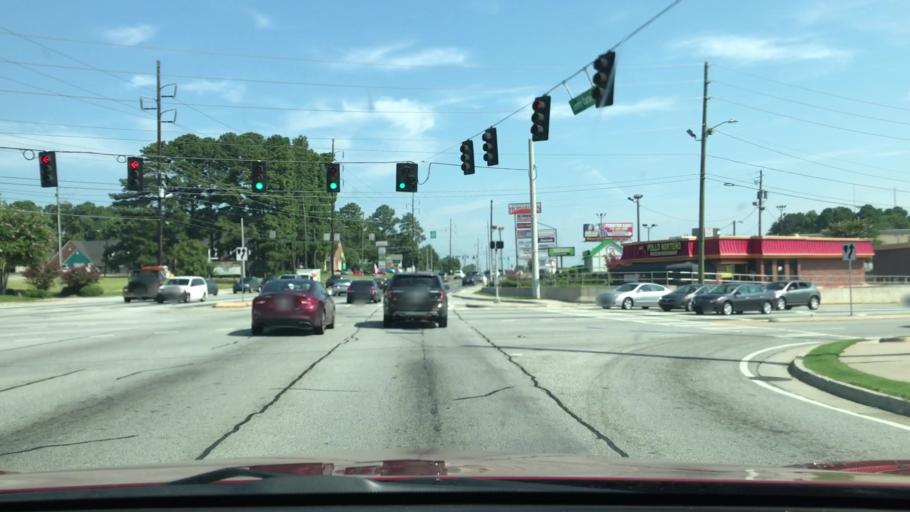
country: US
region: Georgia
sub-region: Gwinnett County
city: Norcross
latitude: 33.9020
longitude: -84.2052
